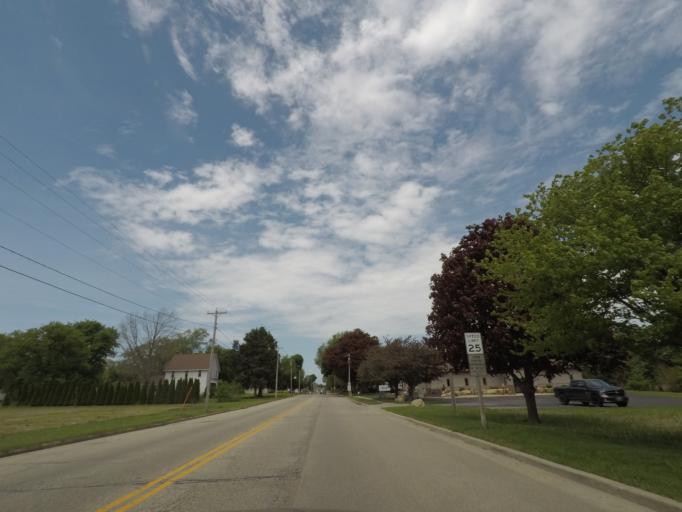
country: US
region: Wisconsin
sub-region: Rock County
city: Orfordville
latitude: 42.6244
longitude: -89.2487
